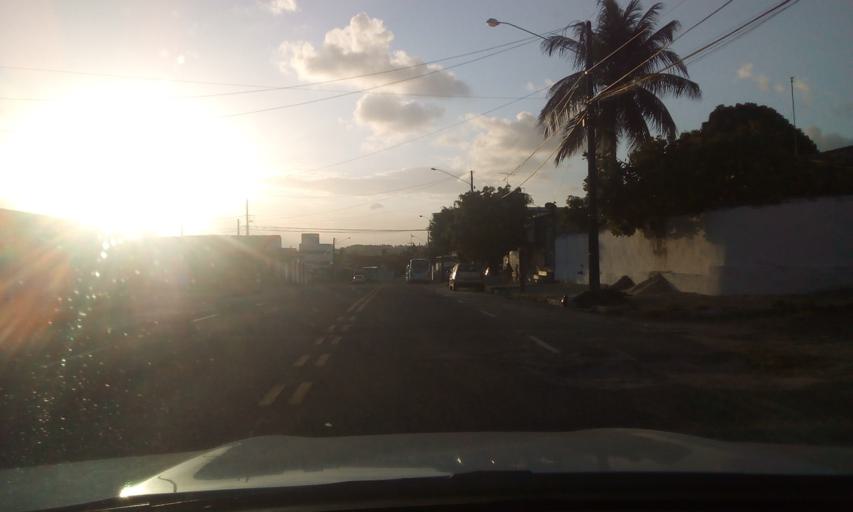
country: BR
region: Paraiba
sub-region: Joao Pessoa
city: Joao Pessoa
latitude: -7.1869
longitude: -34.8453
